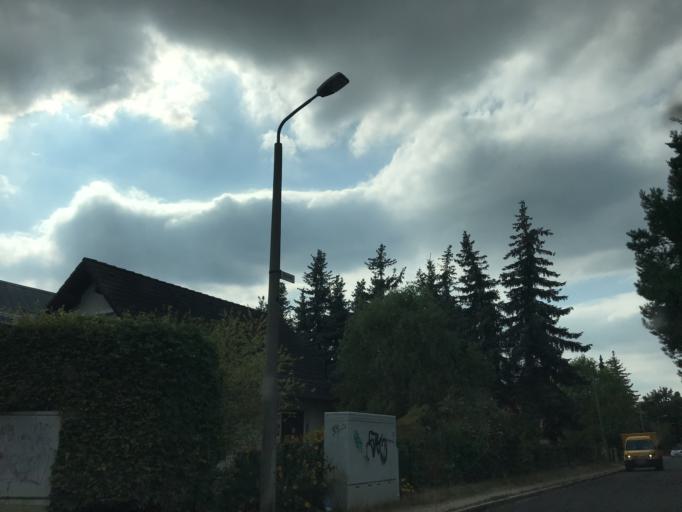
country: DE
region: Brandenburg
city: Kleinmachnow
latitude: 52.4089
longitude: 13.2330
